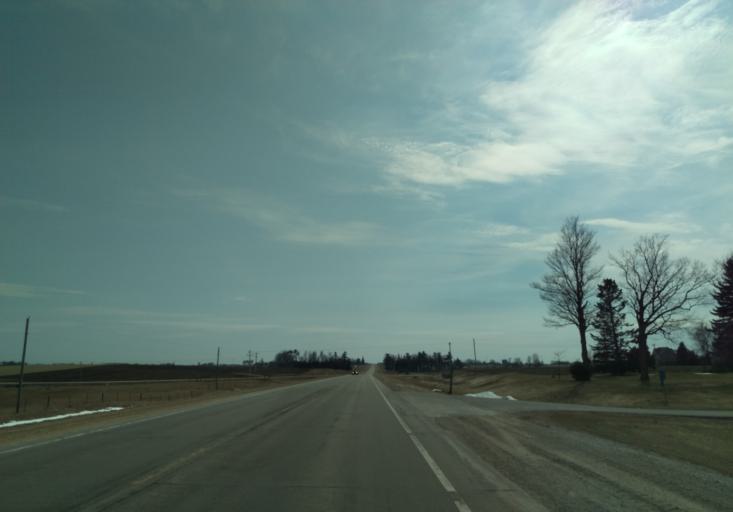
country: US
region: Minnesota
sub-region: Fillmore County
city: Harmony
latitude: 43.4887
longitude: -91.8707
